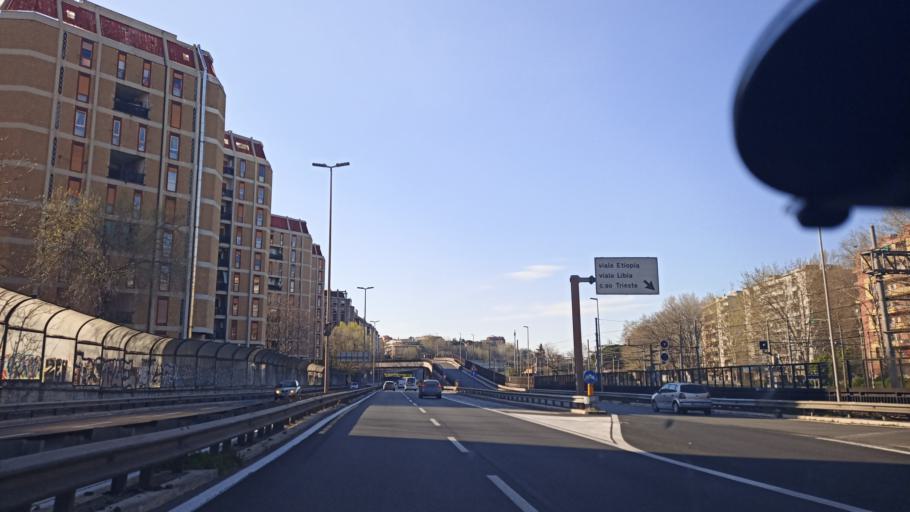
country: IT
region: Latium
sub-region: Citta metropolitana di Roma Capitale
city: Rome
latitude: 41.9310
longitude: 12.5254
